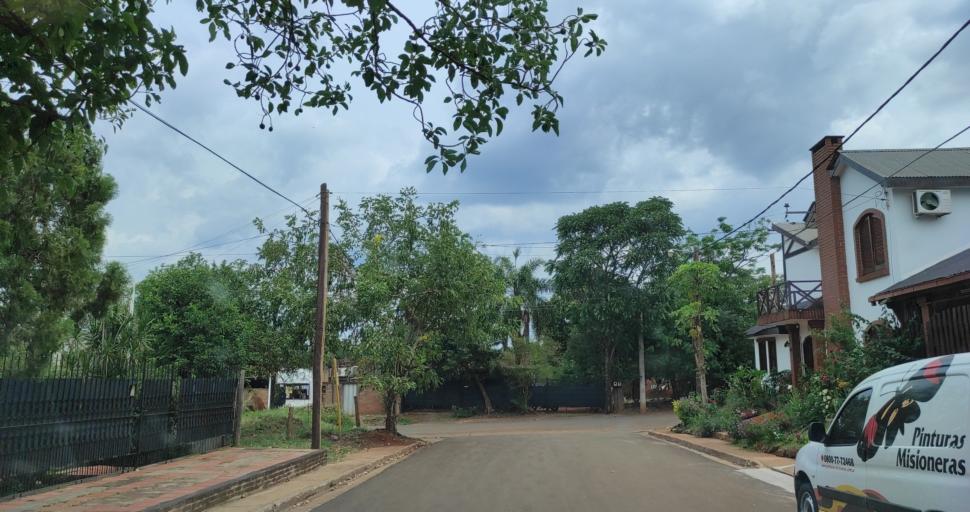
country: AR
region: Misiones
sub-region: Departamento de Capital
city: Posadas
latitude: -27.4094
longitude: -55.9191
